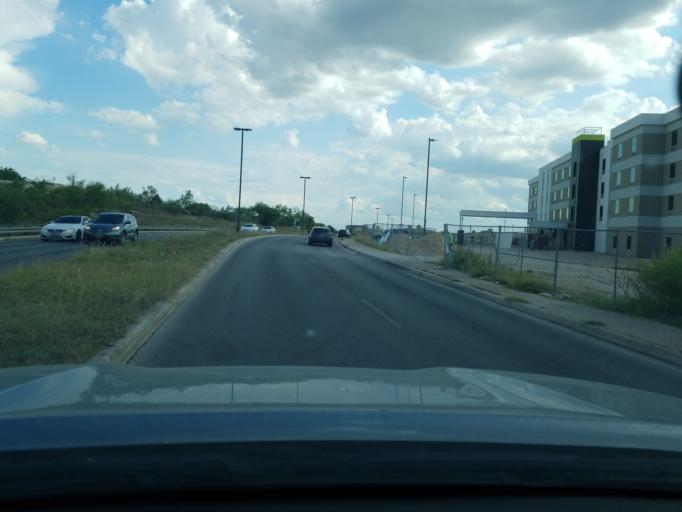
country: US
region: Texas
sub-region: Bexar County
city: Shavano Park
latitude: 29.6043
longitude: -98.5957
